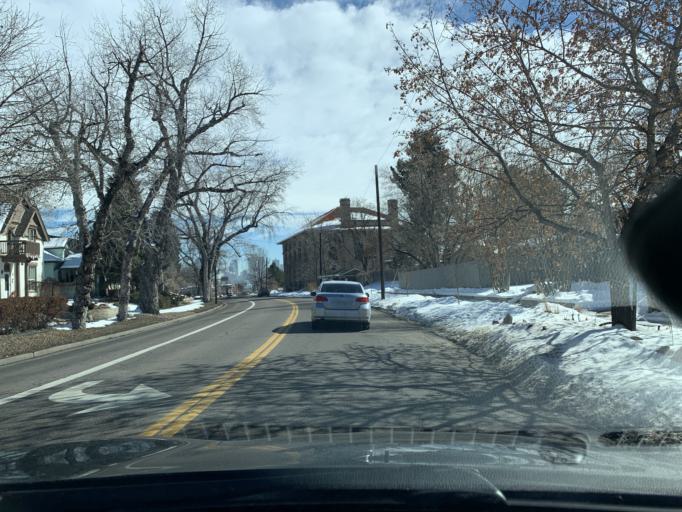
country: US
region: Colorado
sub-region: Jefferson County
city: Edgewater
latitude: 39.7618
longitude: -105.0286
